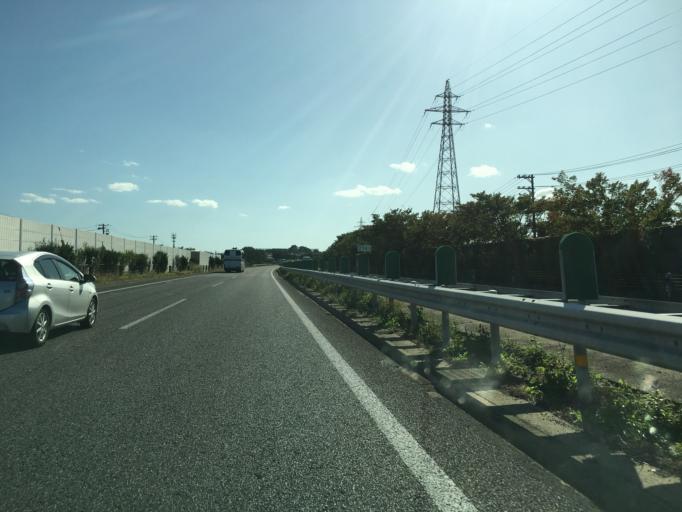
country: JP
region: Fukushima
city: Koriyama
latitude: 37.4211
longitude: 140.3332
